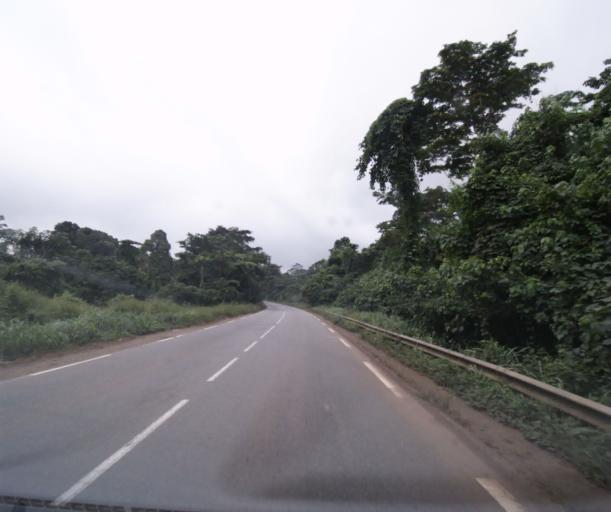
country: CM
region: Centre
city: Eseka
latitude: 3.8735
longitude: 10.6646
